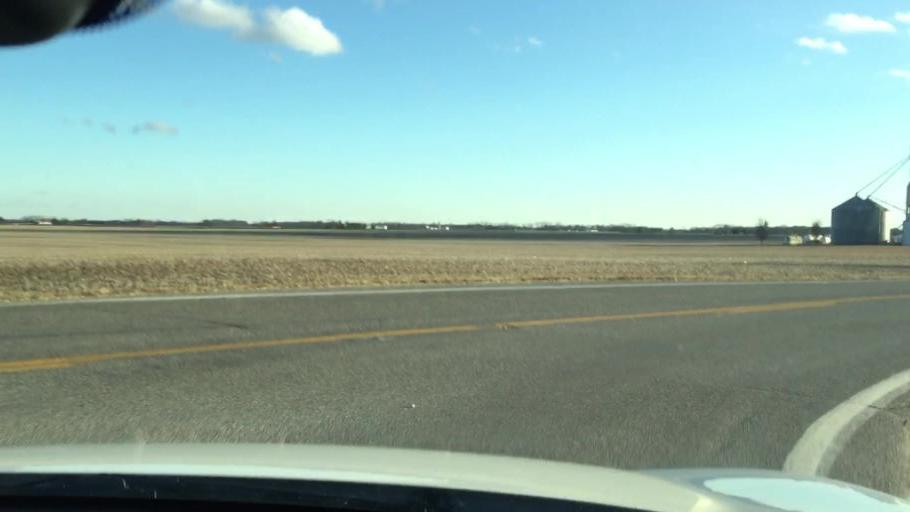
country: US
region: Ohio
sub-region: Champaign County
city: North Lewisburg
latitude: 40.1885
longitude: -83.5179
